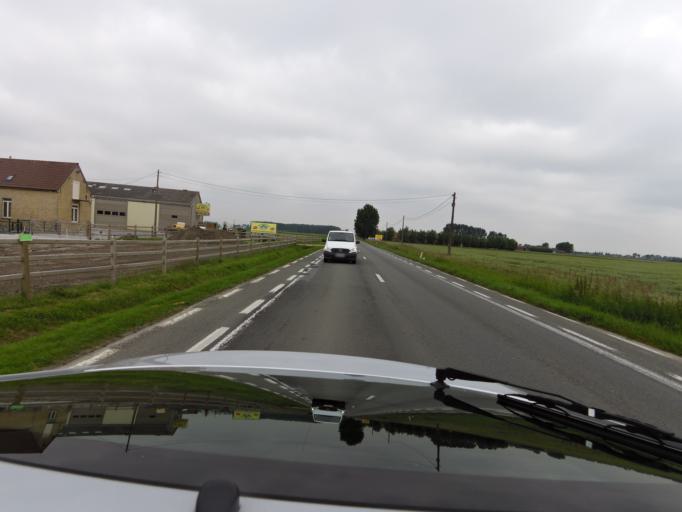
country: BE
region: Flanders
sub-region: Provincie West-Vlaanderen
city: Alveringem
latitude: 51.0281
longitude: 2.6774
